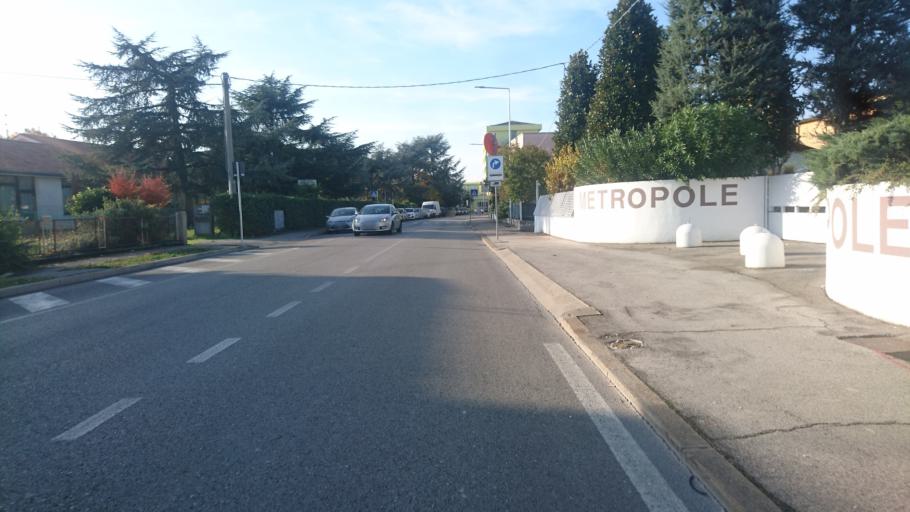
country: IT
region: Veneto
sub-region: Provincia di Padova
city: Abano Terme
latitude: 45.3474
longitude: 11.7906
